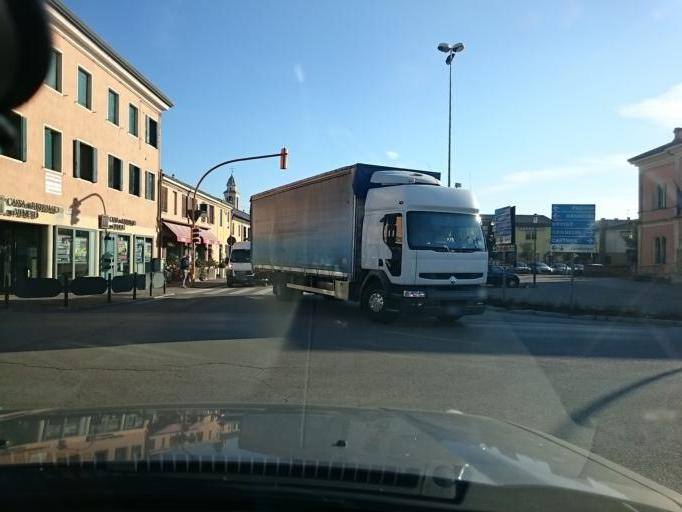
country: IT
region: Veneto
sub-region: Provincia di Padova
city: Masera di Padova
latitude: 45.3204
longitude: 11.8632
